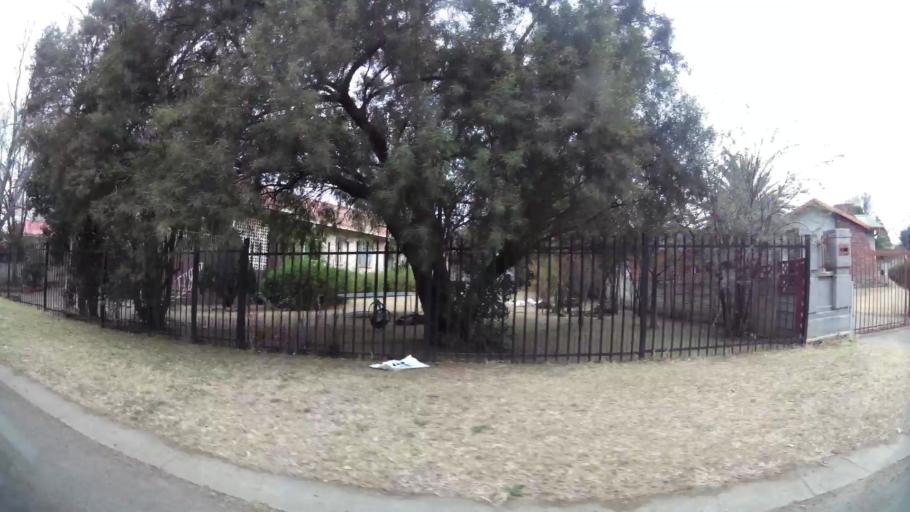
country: ZA
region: Orange Free State
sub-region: Fezile Dabi District Municipality
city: Kroonstad
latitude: -27.6804
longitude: 27.2397
